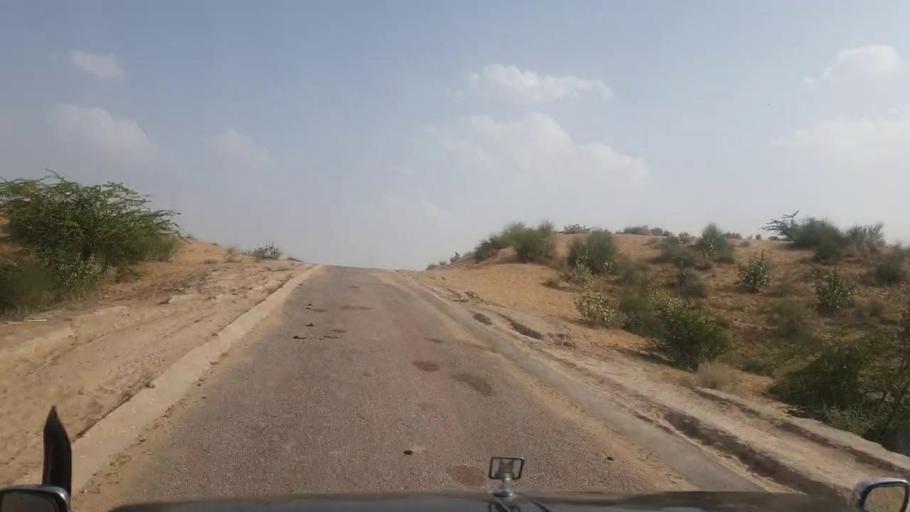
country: PK
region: Sindh
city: Islamkot
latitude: 25.1407
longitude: 70.3168
